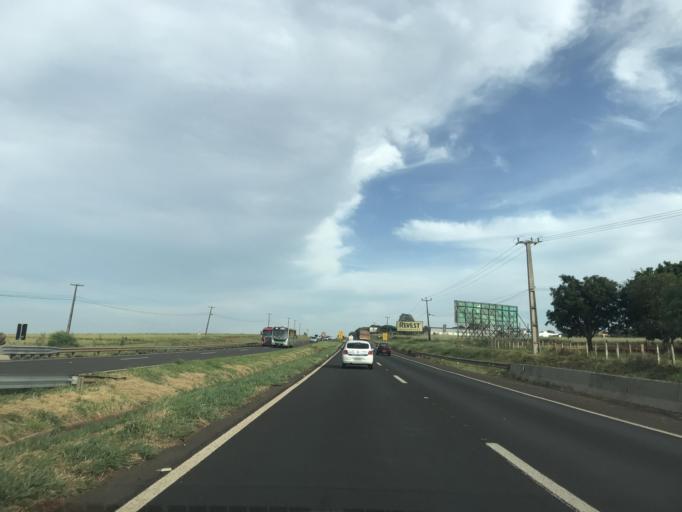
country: BR
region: Parana
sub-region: Paicandu
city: Paicandu
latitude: -23.3943
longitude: -52.0083
